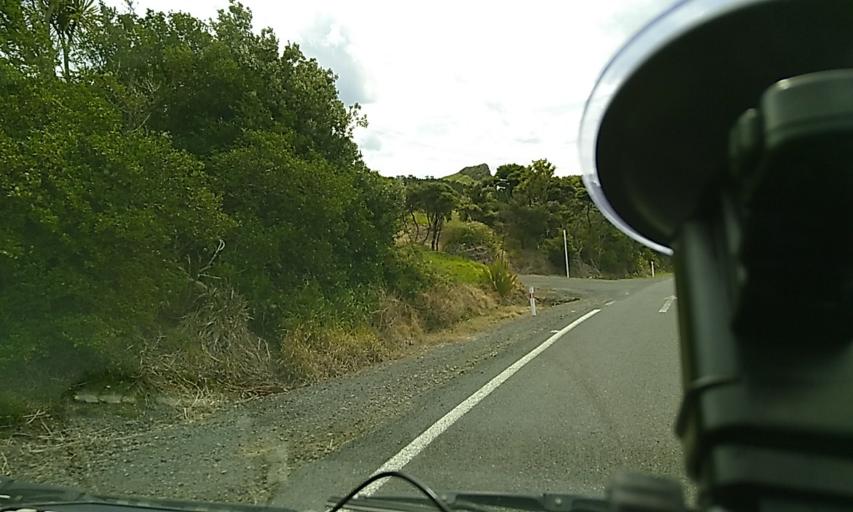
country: NZ
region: Northland
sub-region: Far North District
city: Ahipara
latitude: -35.5407
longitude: 173.3868
